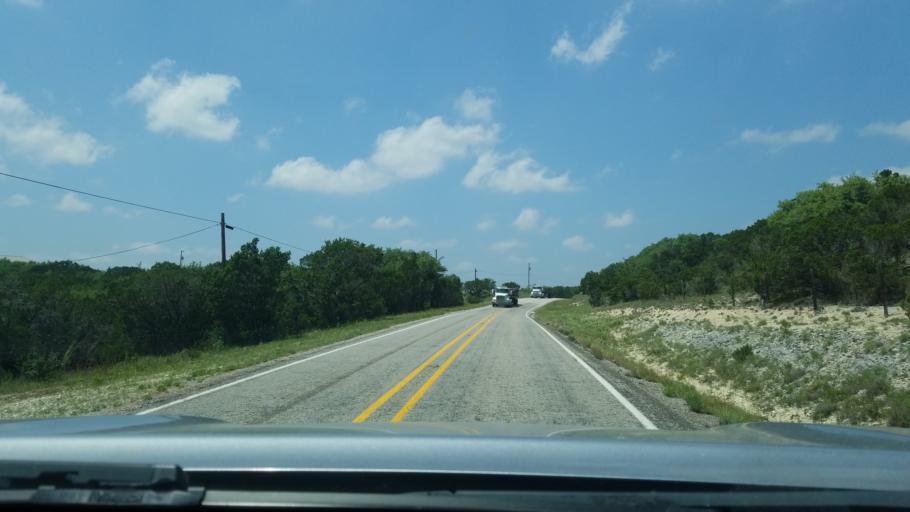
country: US
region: Texas
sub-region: Hays County
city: Woodcreek
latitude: 30.0792
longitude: -98.2245
